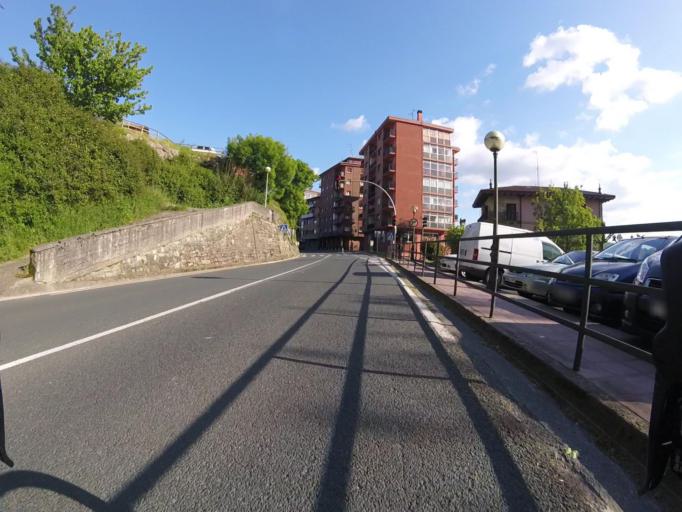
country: ES
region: Basque Country
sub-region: Provincia de Guipuzcoa
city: Lezo
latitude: 43.3232
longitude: -1.9006
